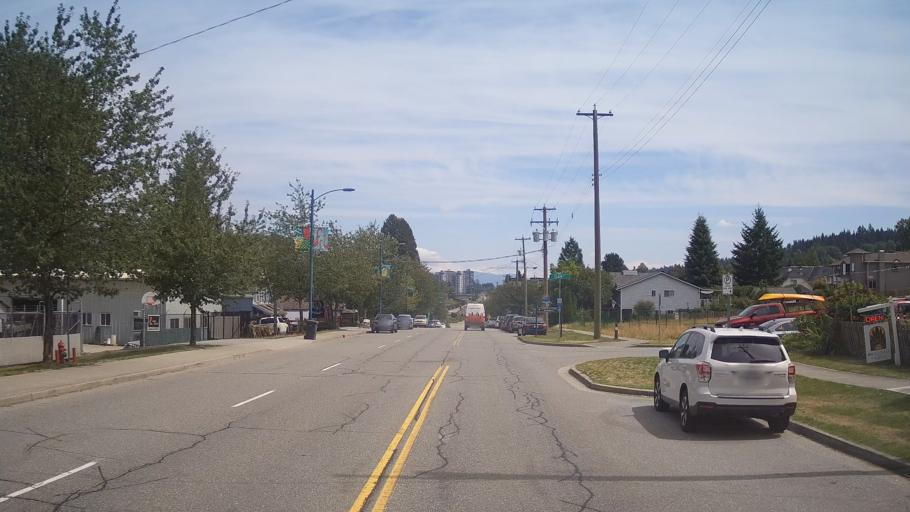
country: CA
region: British Columbia
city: Port Moody
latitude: 49.2779
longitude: -122.8609
